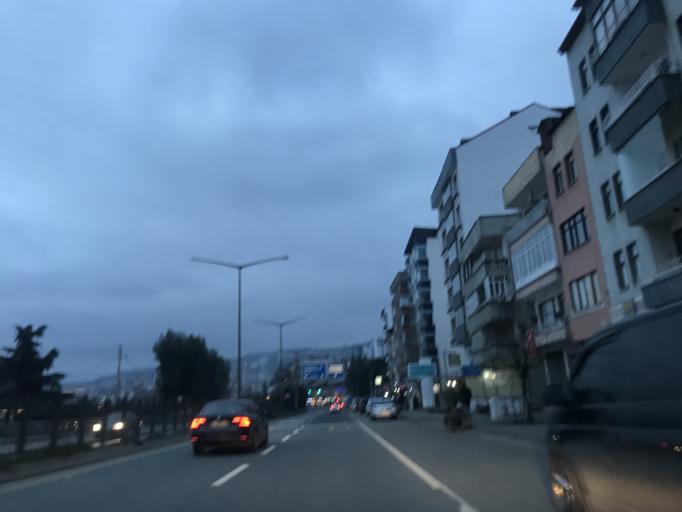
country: TR
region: Trabzon
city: Akcaabat
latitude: 41.0273
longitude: 39.5639
